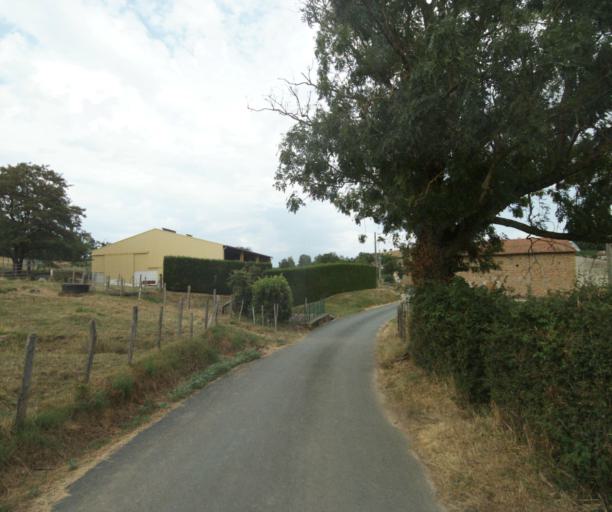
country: FR
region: Rhone-Alpes
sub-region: Departement du Rhone
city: Bully
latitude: 45.8714
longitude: 4.5722
